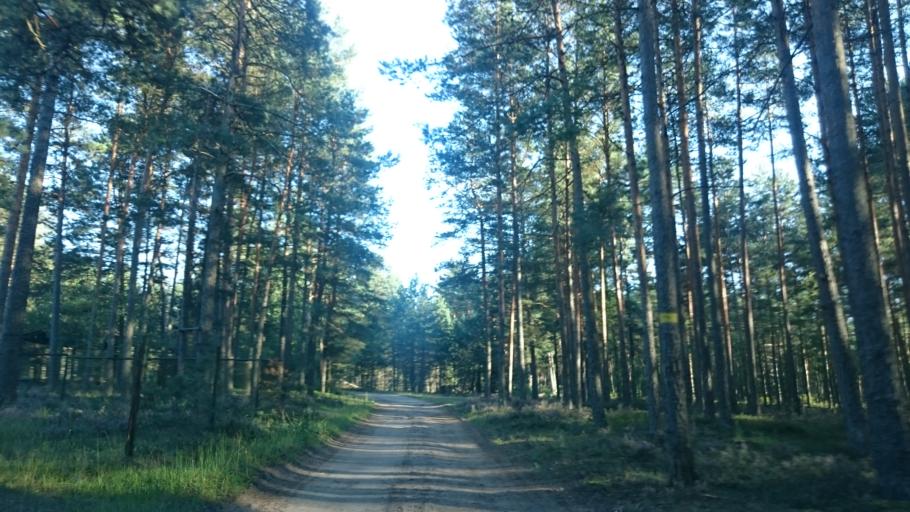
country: LV
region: Carnikava
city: Carnikava
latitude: 57.1029
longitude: 24.2318
